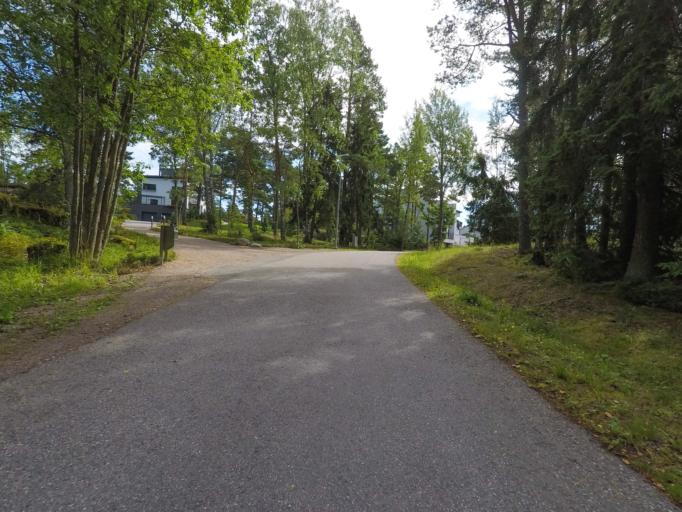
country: FI
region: Uusimaa
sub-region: Helsinki
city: Vantaa
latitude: 60.1628
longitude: 25.0880
